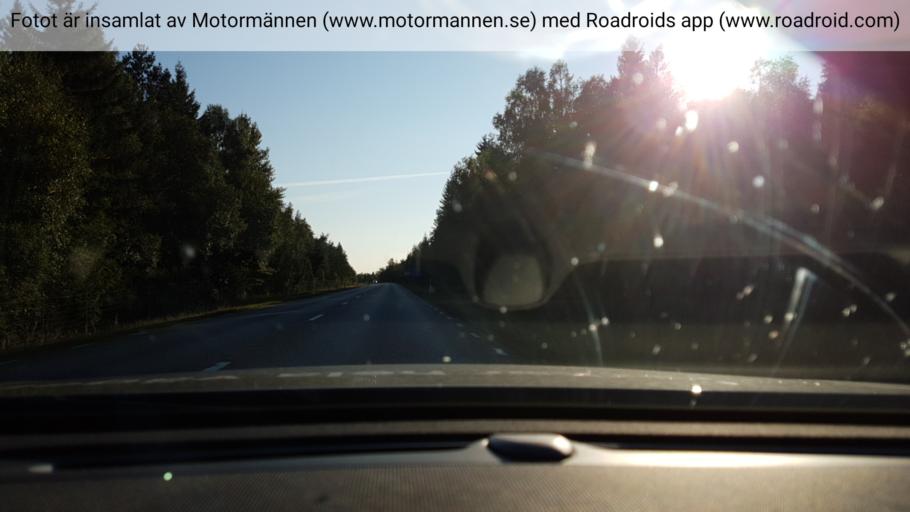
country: SE
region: Halland
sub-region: Hylte Kommun
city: Hyltebruk
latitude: 57.0539
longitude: 13.3307
